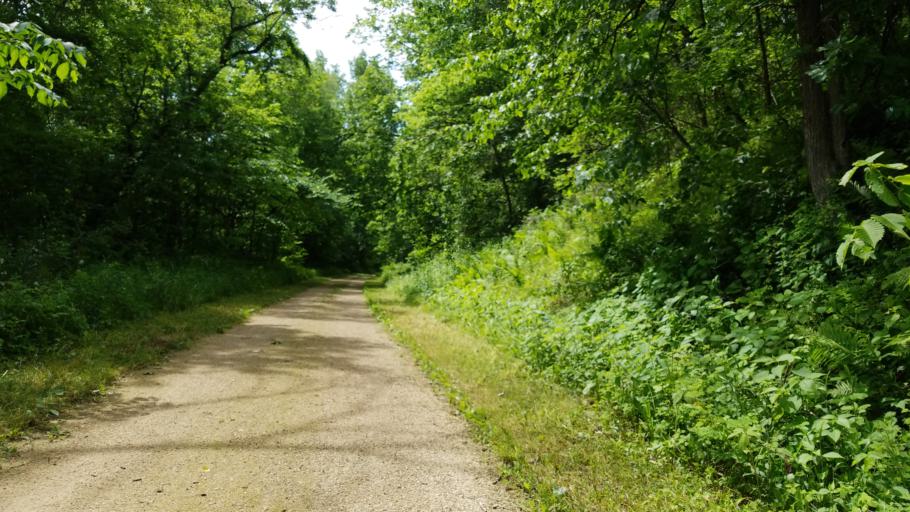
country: US
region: Wisconsin
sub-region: Dunn County
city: Menomonie
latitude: 44.8081
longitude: -91.9478
